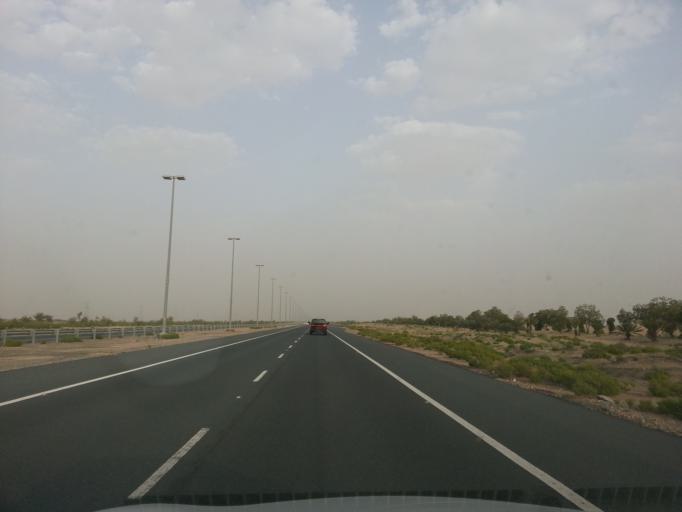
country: AE
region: Dubai
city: Dubai
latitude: 24.5935
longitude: 55.1418
